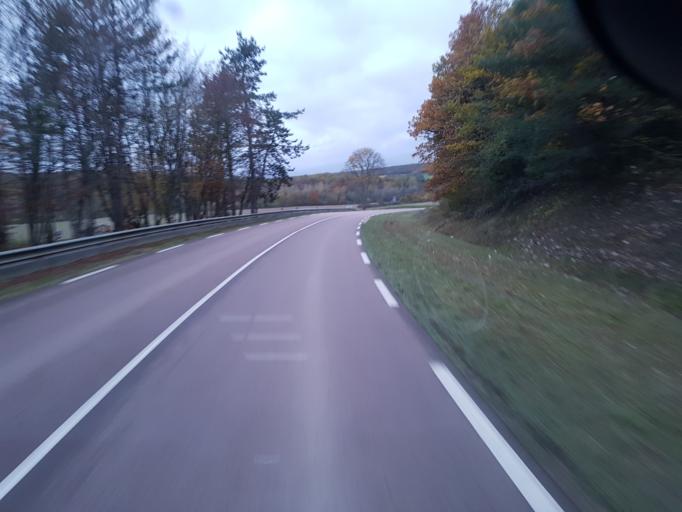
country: FR
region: Champagne-Ardenne
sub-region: Departement de l'Aube
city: Mussy-sur-Seine
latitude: 48.0009
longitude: 4.4747
